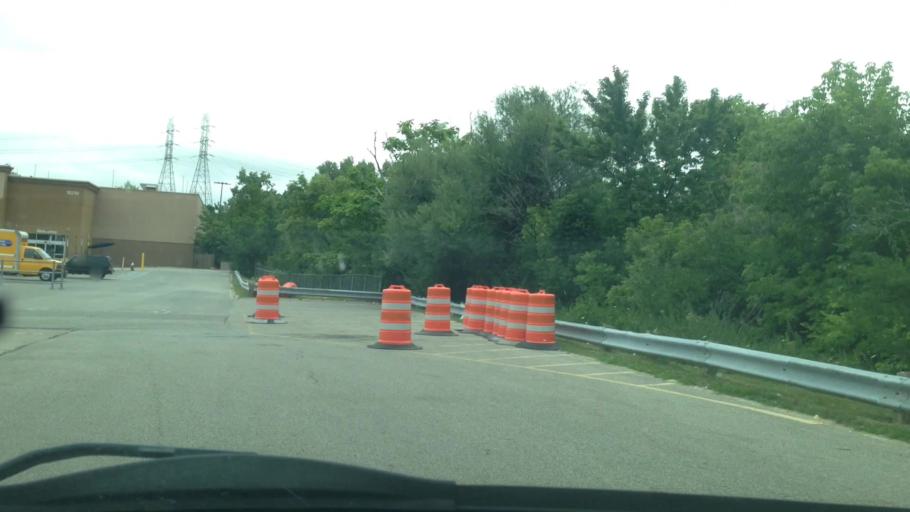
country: US
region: Ohio
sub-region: Cuyahoga County
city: Brooklyn
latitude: 41.4192
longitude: -81.7558
